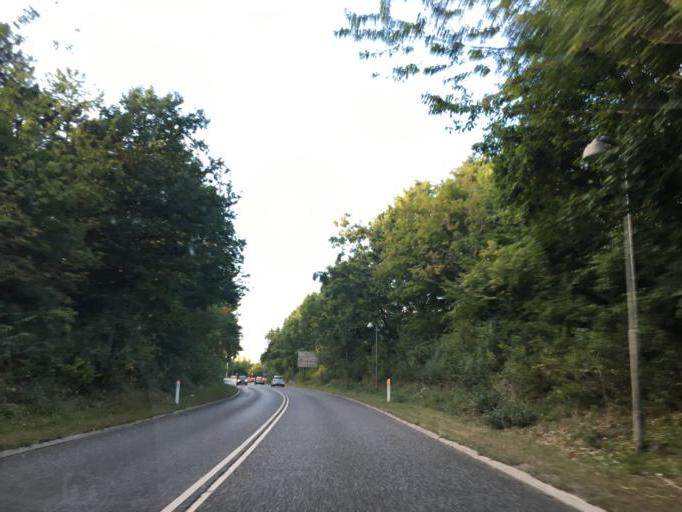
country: DK
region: Capital Region
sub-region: Horsholm Kommune
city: Horsholm
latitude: 55.8760
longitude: 12.4964
